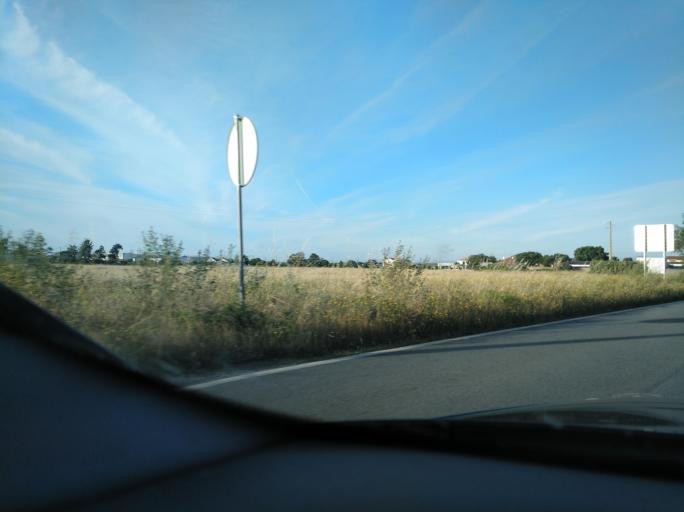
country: PT
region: Setubal
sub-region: Montijo
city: Montijo
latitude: 38.7081
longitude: -8.9030
